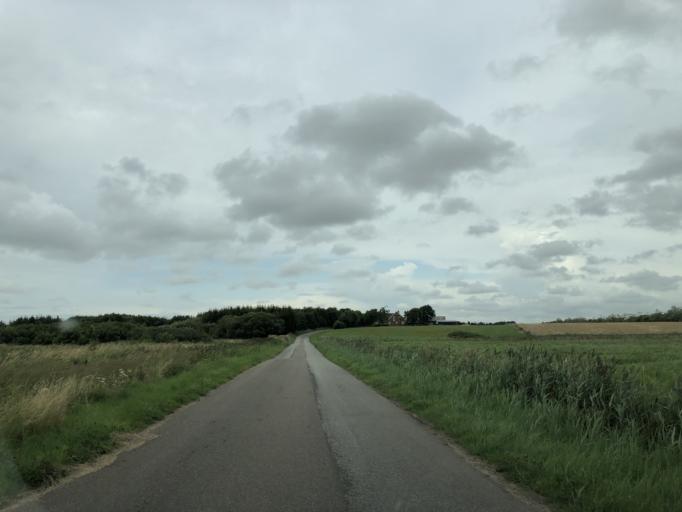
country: DK
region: Central Jutland
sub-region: Ringkobing-Skjern Kommune
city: Ringkobing
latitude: 56.1345
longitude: 8.2688
